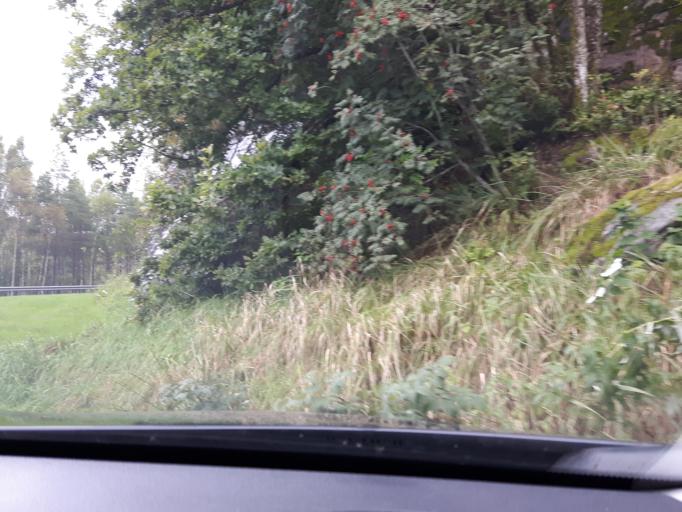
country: NO
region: Vest-Agder
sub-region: Marnardal
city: Helland
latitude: 58.0871
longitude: 7.6211
